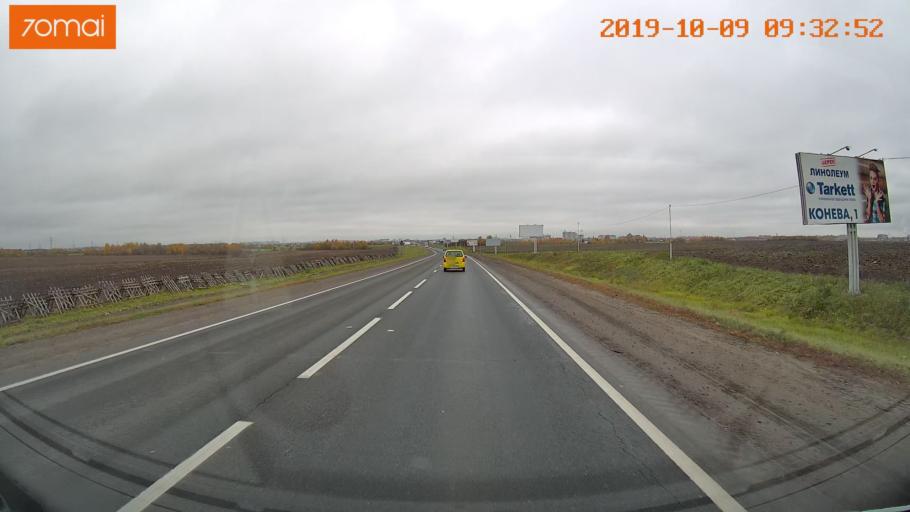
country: RU
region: Vologda
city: Vologda
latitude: 59.1633
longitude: 39.9228
